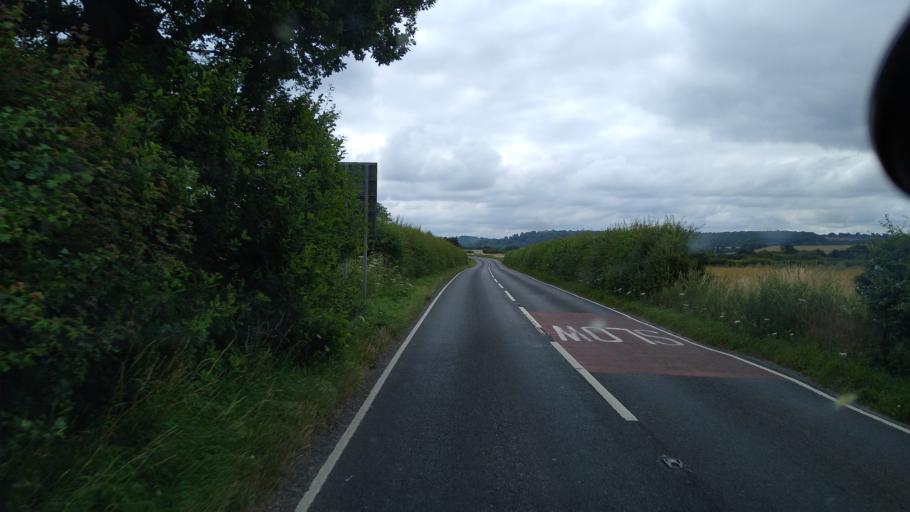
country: GB
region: England
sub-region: Hampshire
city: Alton
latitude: 51.1226
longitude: -0.9509
